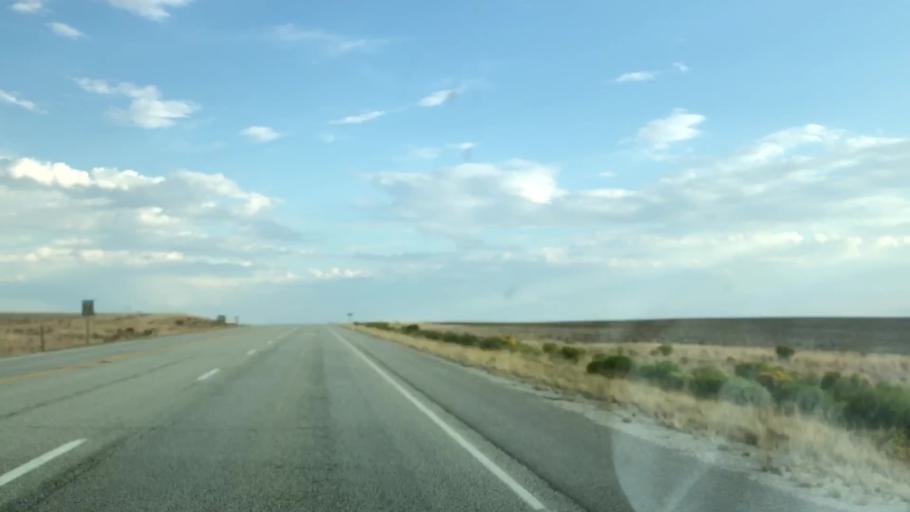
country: US
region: Wyoming
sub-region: Sweetwater County
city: North Rock Springs
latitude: 42.2652
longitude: -109.4752
